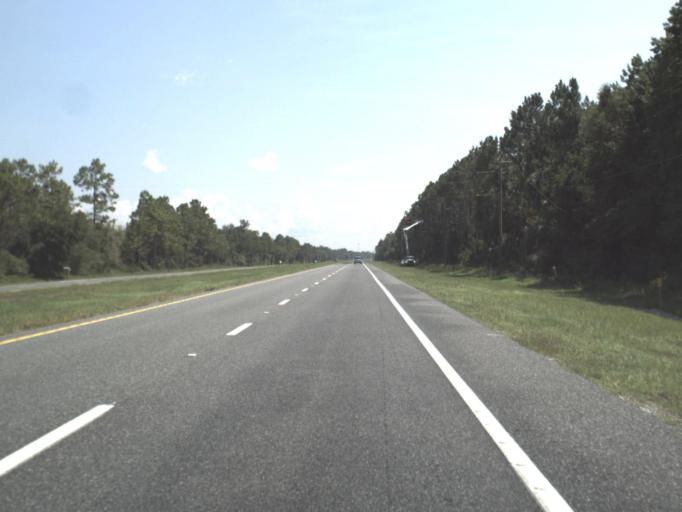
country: US
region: Florida
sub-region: Levy County
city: Inglis
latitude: 29.1426
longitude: -82.6379
